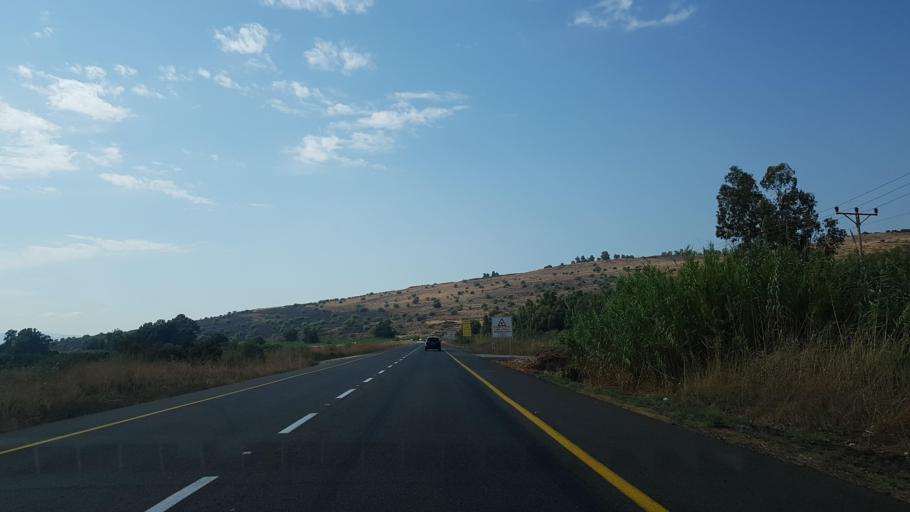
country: SY
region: Quneitra
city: Al Butayhah
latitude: 32.9044
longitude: 35.6230
